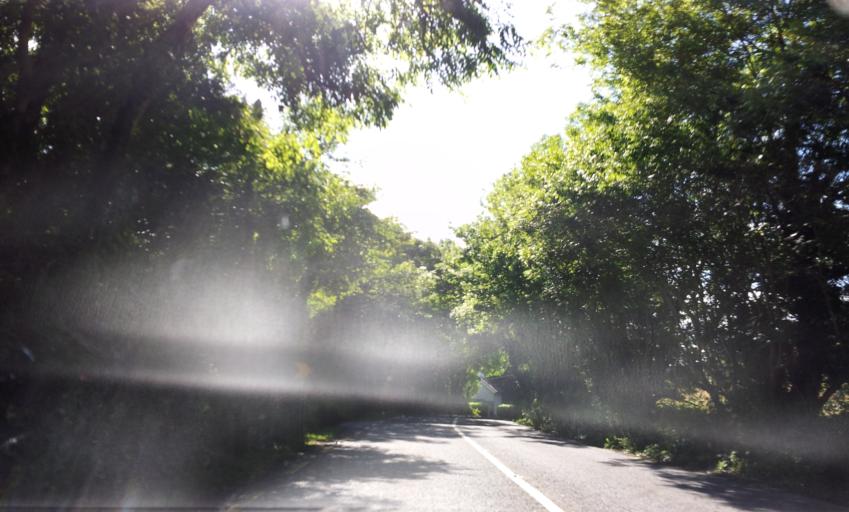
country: IE
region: Munster
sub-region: County Cork
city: Millstreet
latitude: 51.9255
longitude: -9.1070
